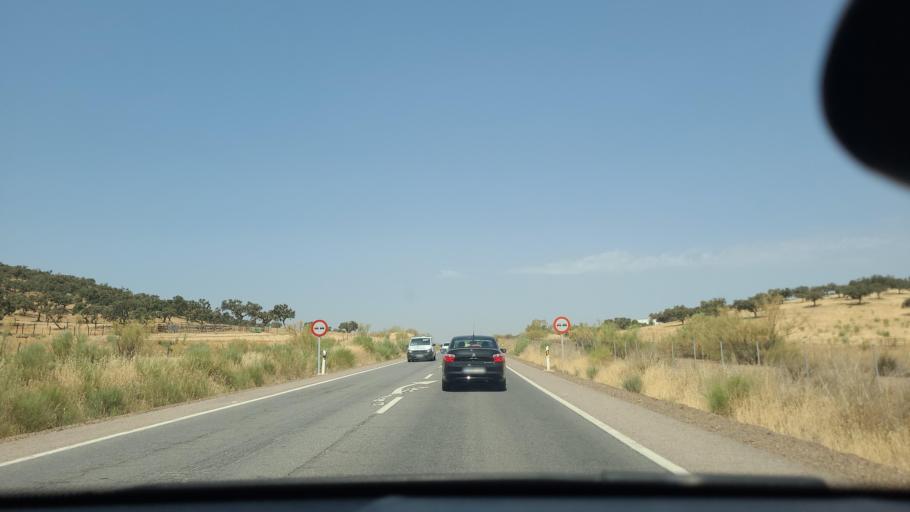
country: ES
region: Extremadura
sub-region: Provincia de Badajoz
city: Fuente del Maestre
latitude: 38.4707
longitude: -6.4475
